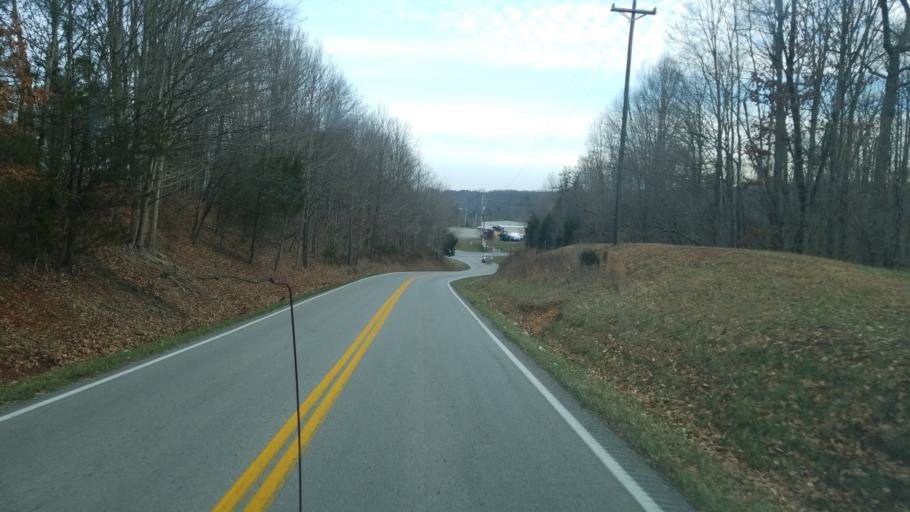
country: US
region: Kentucky
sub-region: Clinton County
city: Albany
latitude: 36.7520
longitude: -85.1190
